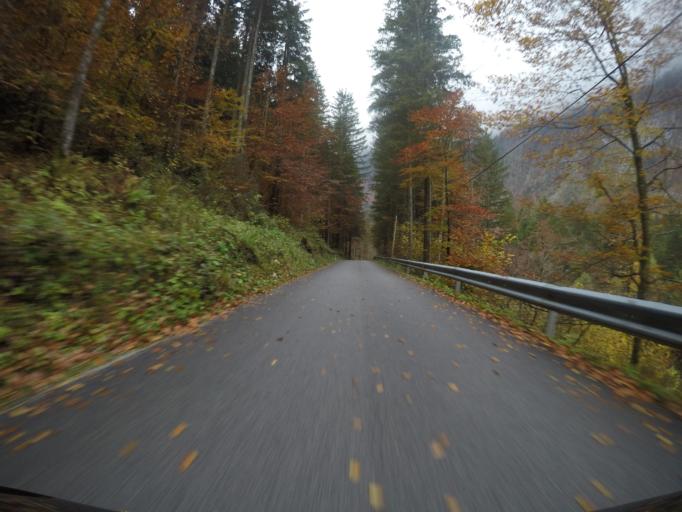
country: SI
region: Jesenice
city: Hrusica
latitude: 46.3996
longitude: 14.0010
